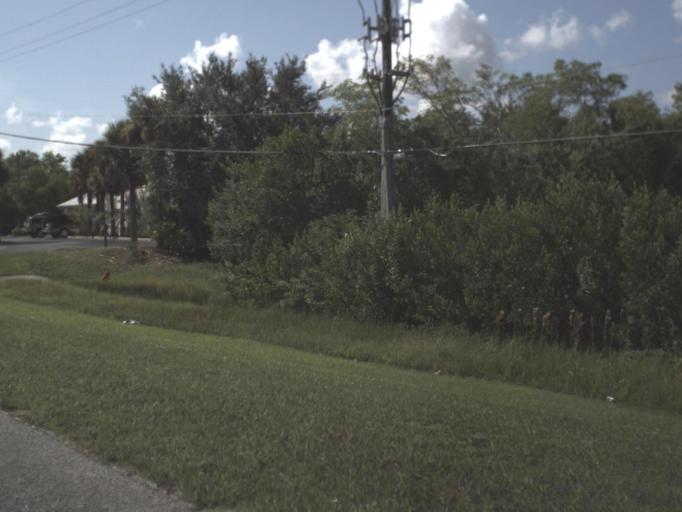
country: US
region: Florida
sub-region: Charlotte County
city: Charlotte Park
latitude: 26.9057
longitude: -82.0377
